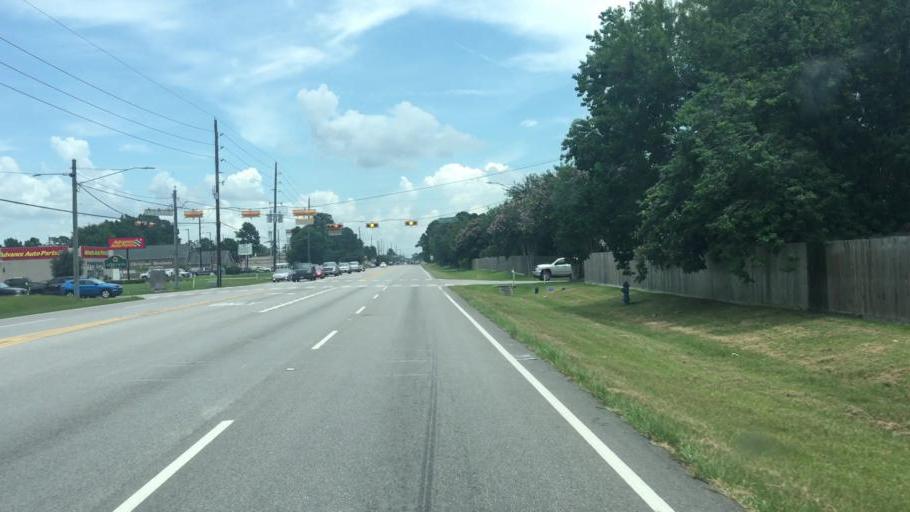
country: US
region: Texas
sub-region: Harris County
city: Atascocita
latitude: 29.9944
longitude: -95.1747
